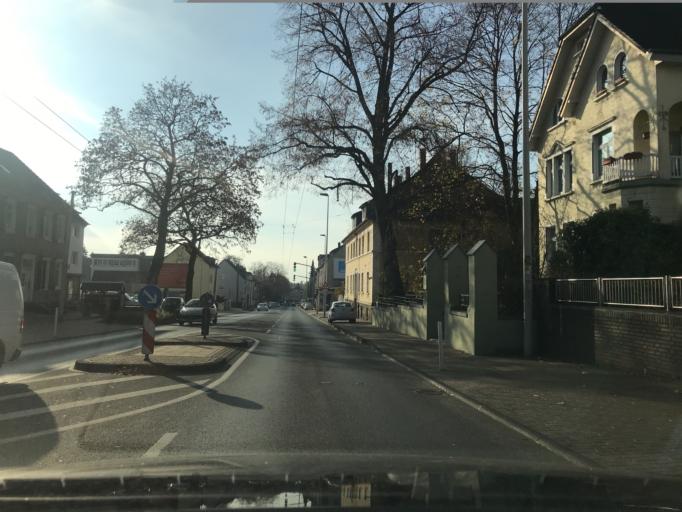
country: DE
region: North Rhine-Westphalia
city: Haan
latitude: 51.1744
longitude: 7.0224
